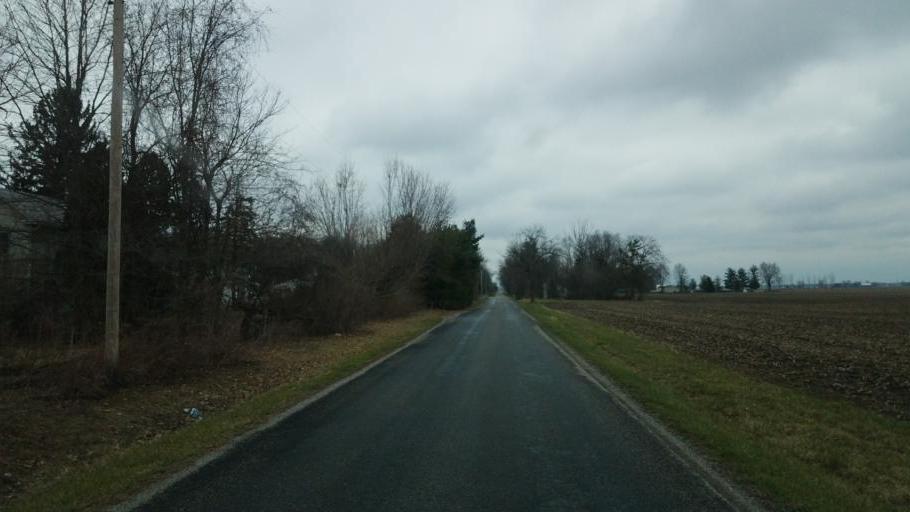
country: US
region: Ohio
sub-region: Delaware County
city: Ashley
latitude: 40.3661
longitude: -82.9870
